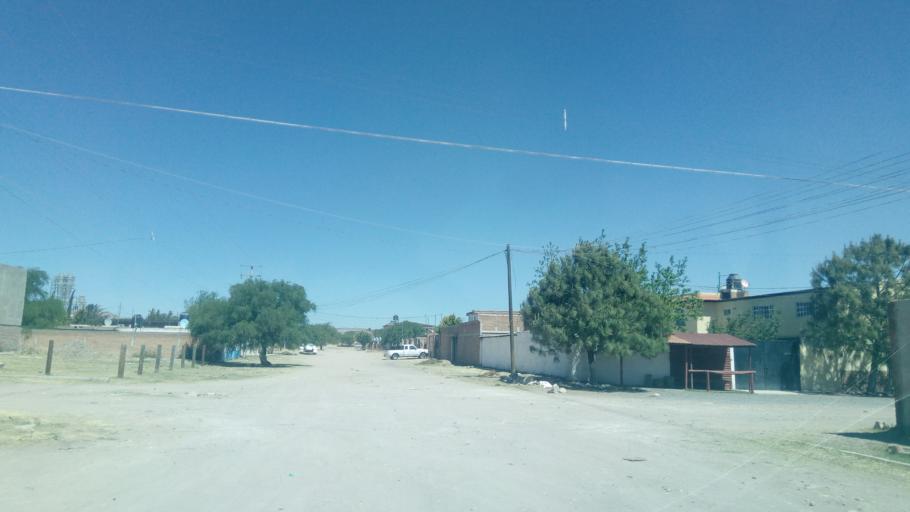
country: MX
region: Durango
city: Victoria de Durango
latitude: 24.0779
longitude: -104.6585
